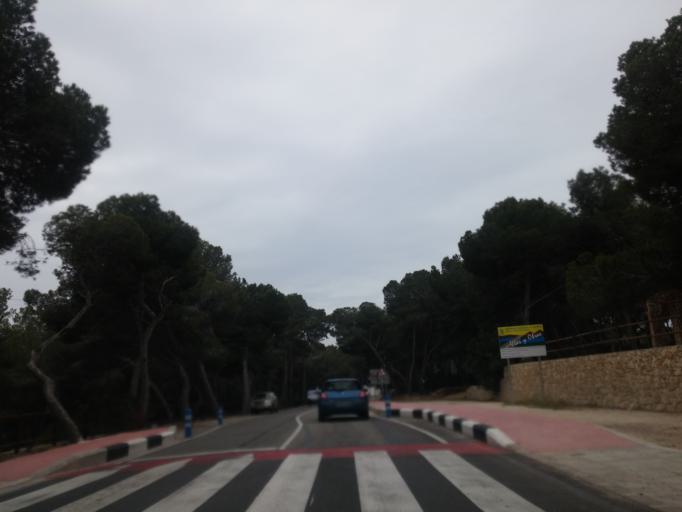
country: ES
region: Valencia
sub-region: Provincia de Alicante
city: Moraira
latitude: 38.6703
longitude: 0.0920
